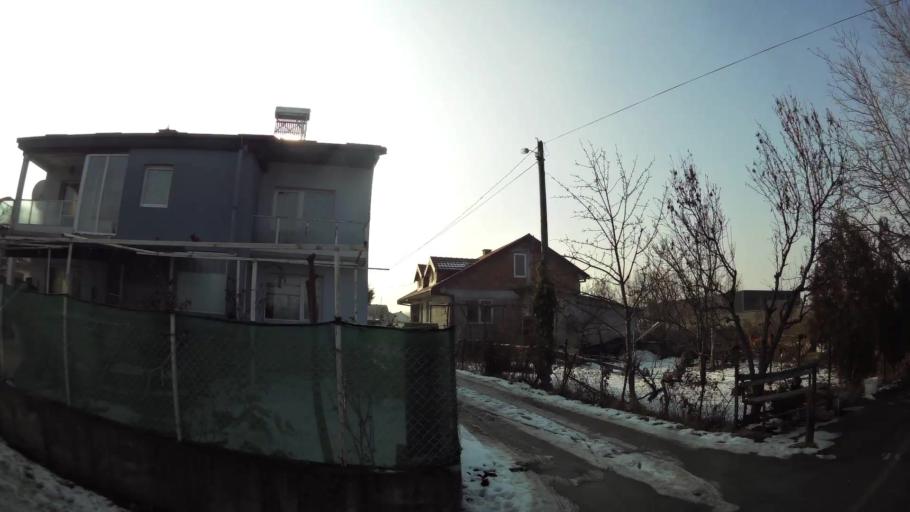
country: MK
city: Kadino
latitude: 41.9602
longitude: 21.6012
